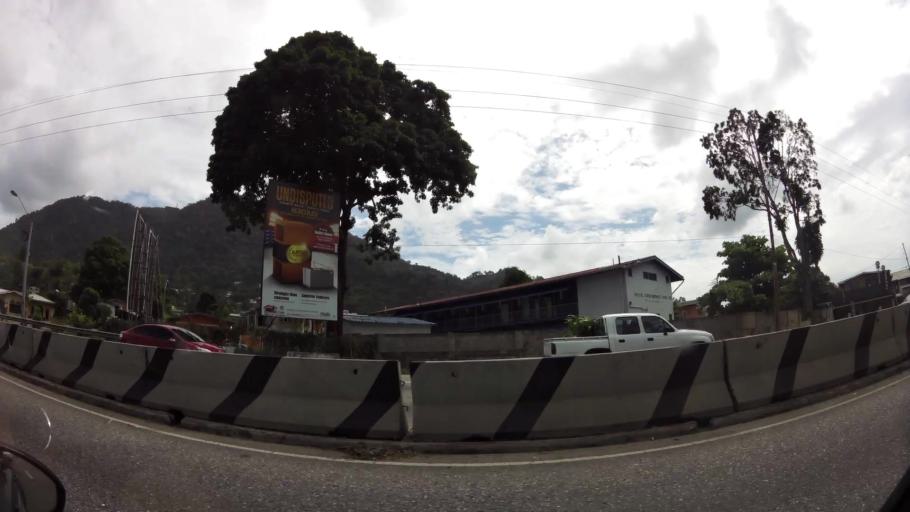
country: TT
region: Diego Martin
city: Petit Valley
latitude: 10.7001
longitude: -61.5534
